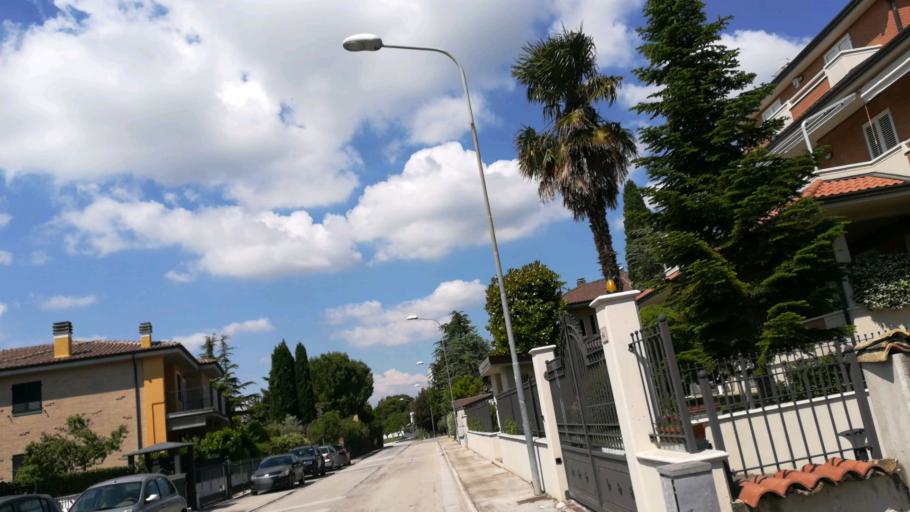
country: IT
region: The Marches
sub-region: Provincia di Macerata
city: Borgo Stazione
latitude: 43.2825
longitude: 13.6425
